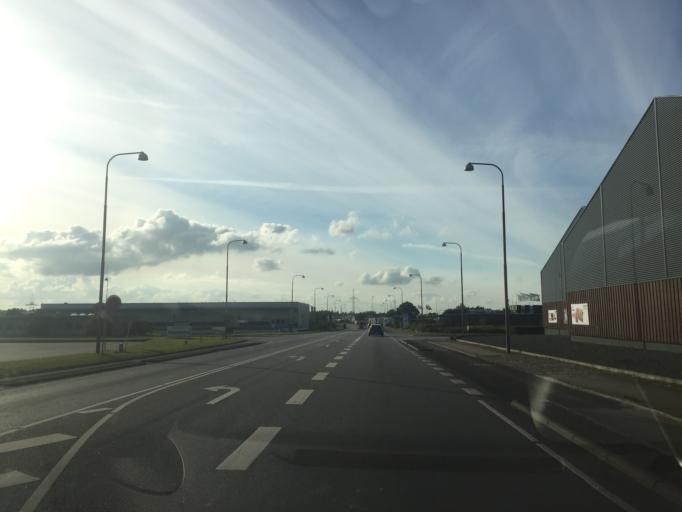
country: DK
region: South Denmark
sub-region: Aabenraa Kommune
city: Padborg
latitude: 54.8327
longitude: 9.3497
